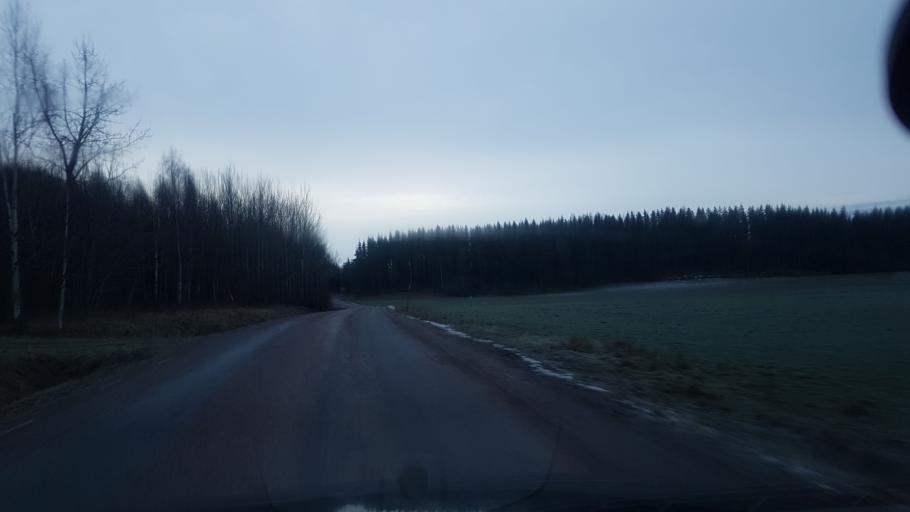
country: SE
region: Dalarna
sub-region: Borlange Kommun
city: Ornas
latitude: 60.4402
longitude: 15.6470
